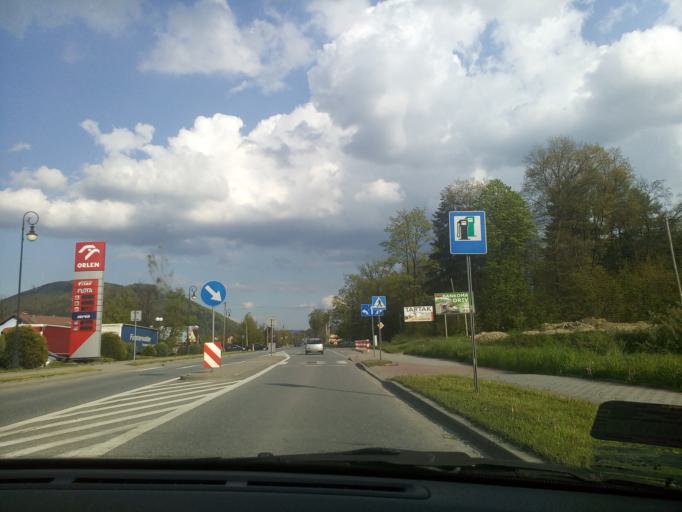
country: PL
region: Lesser Poland Voivodeship
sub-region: Powiat nowosadecki
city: Nawojowa
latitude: 49.5570
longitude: 20.7502
